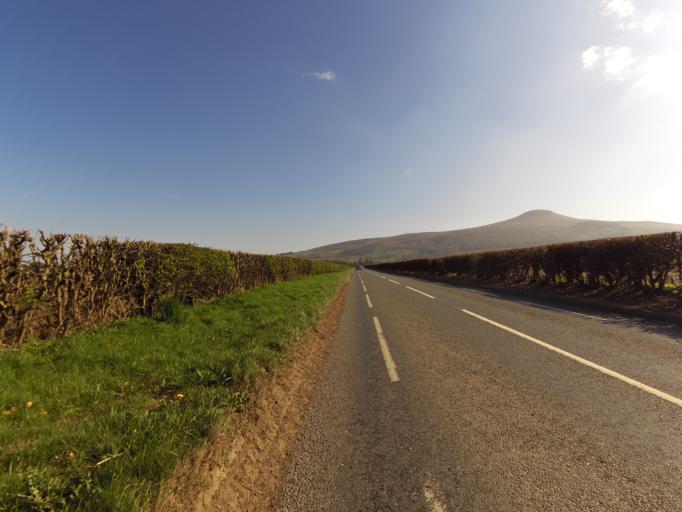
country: GB
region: Scotland
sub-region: Fife
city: Falkland
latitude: 56.2636
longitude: -3.2086
